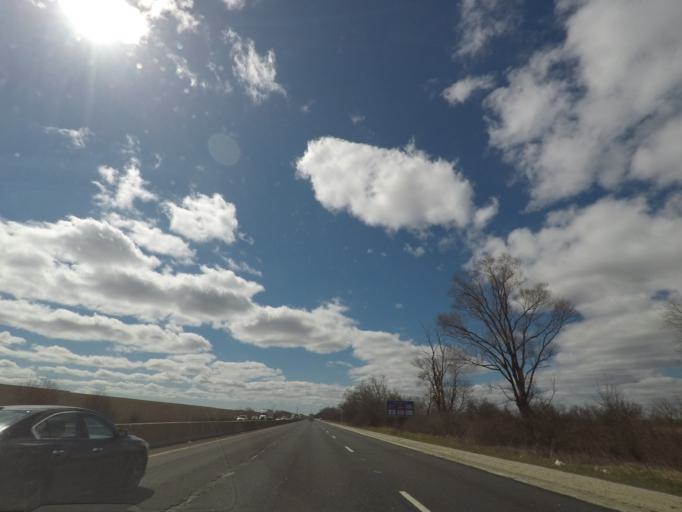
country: US
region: Illinois
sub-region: Will County
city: Crystal Lawns
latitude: 41.6074
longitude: -88.1634
